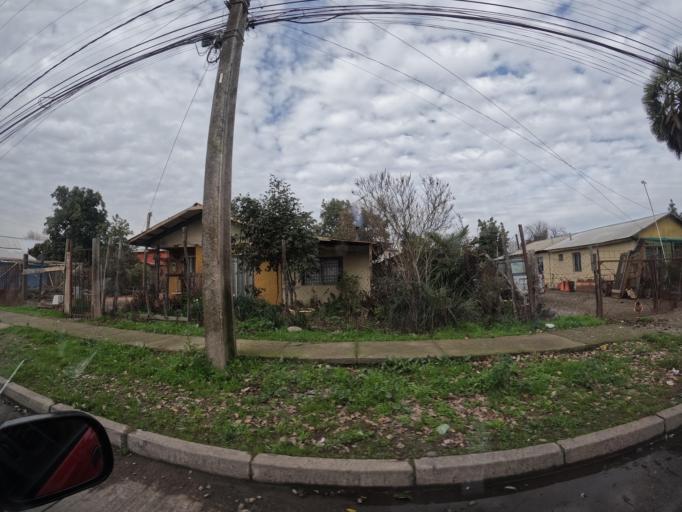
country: CL
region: Maule
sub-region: Provincia de Linares
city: Linares
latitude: -35.8533
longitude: -71.6110
